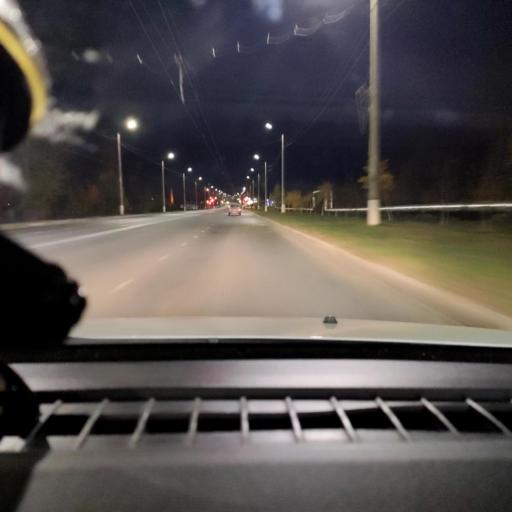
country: RU
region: Samara
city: Novokuybyshevsk
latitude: 53.0995
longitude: 49.9396
